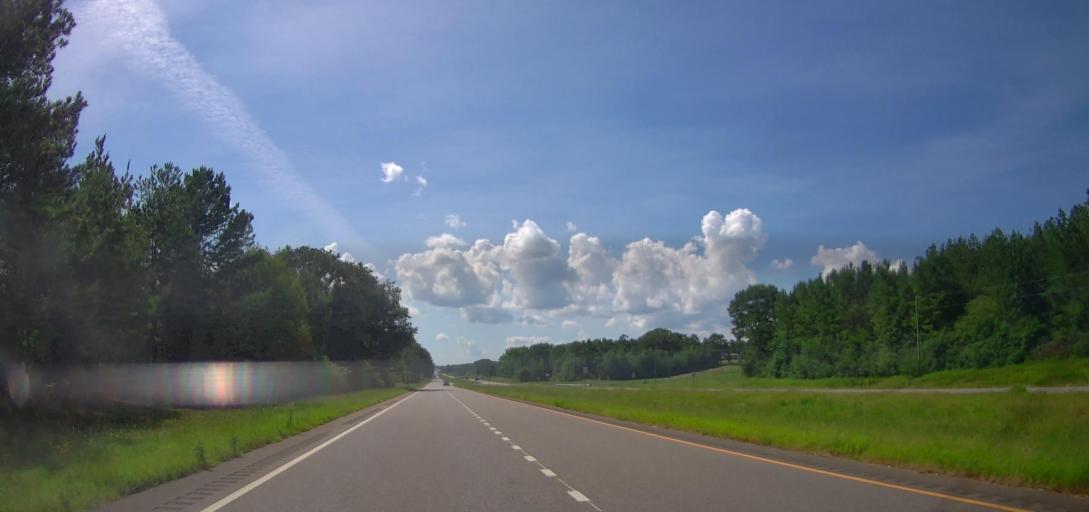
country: US
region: Alabama
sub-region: Pickens County
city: Gordo
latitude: 33.3387
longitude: -87.9364
